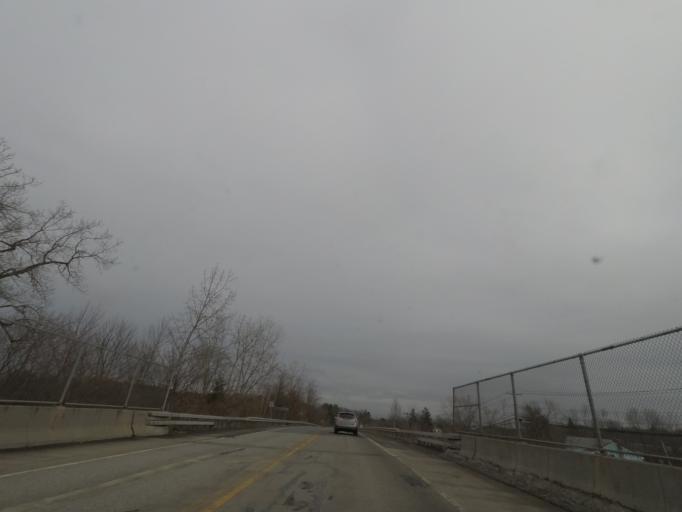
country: US
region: New York
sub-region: Albany County
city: Voorheesville
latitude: 42.7028
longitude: -73.9576
